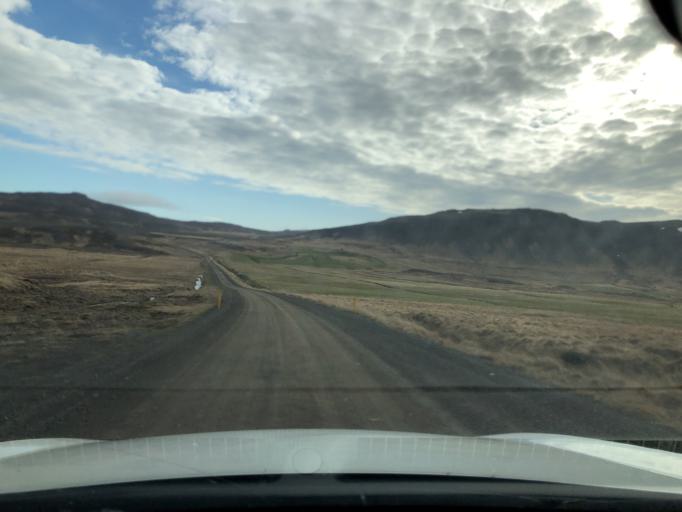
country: IS
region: West
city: Stykkisholmur
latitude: 65.0149
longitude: -22.5639
